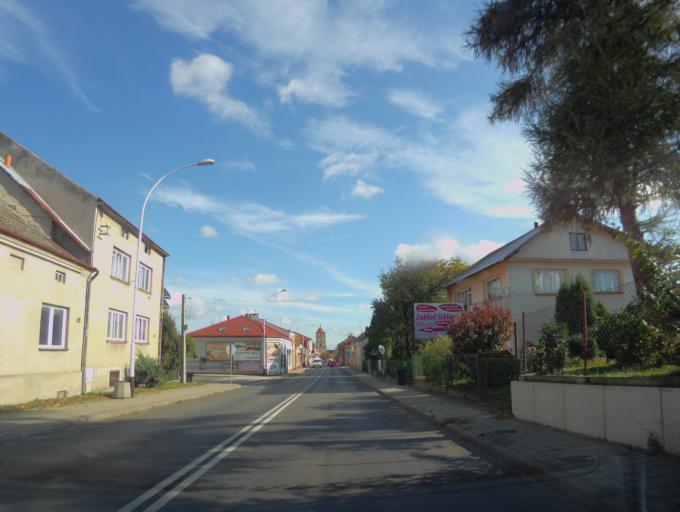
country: PL
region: Subcarpathian Voivodeship
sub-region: Powiat lezajski
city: Lezajsk
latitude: 50.2514
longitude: 22.4188
